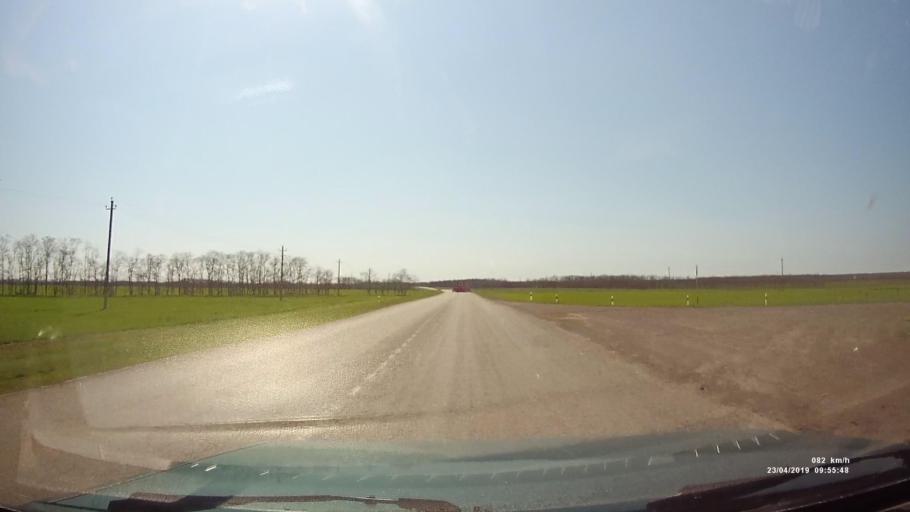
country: RU
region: Rostov
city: Orlovskiy
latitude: 46.8044
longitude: 42.0656
